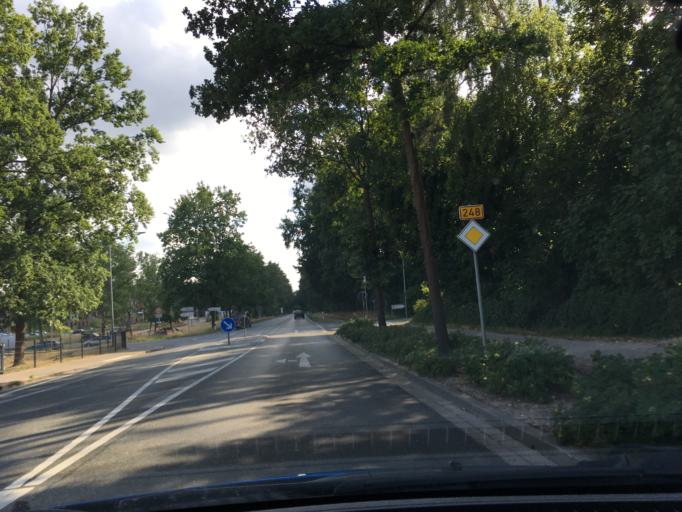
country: DE
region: Lower Saxony
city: Dannenberg
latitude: 53.0851
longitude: 11.0806
